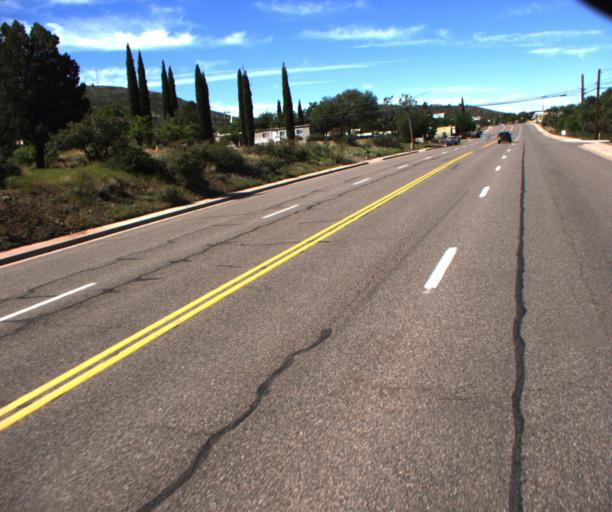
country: US
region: Arizona
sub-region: Yavapai County
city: Congress
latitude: 34.2257
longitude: -112.7440
